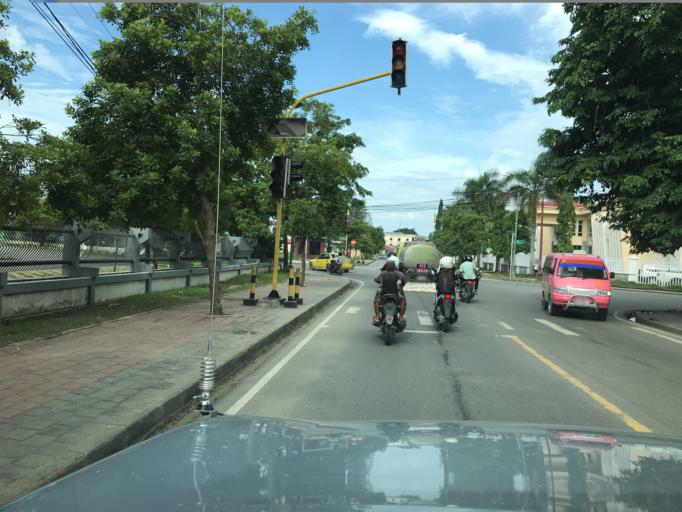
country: TL
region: Dili
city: Dili
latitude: -8.5570
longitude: 125.5684
